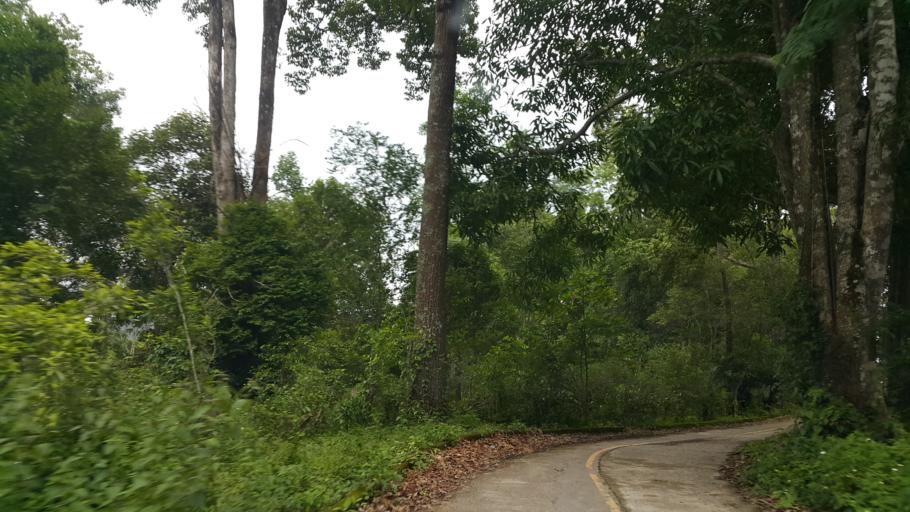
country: TH
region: Lampang
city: Mueang Pan
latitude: 18.8328
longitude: 99.3777
